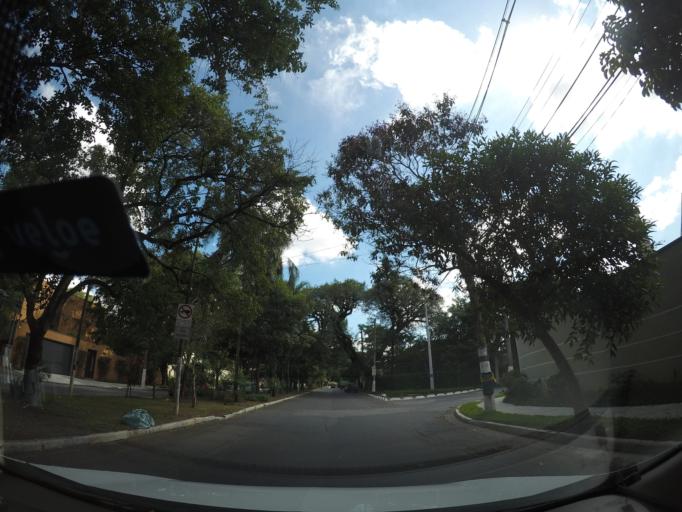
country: BR
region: Sao Paulo
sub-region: Sao Paulo
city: Sao Paulo
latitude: -23.5571
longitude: -46.7082
